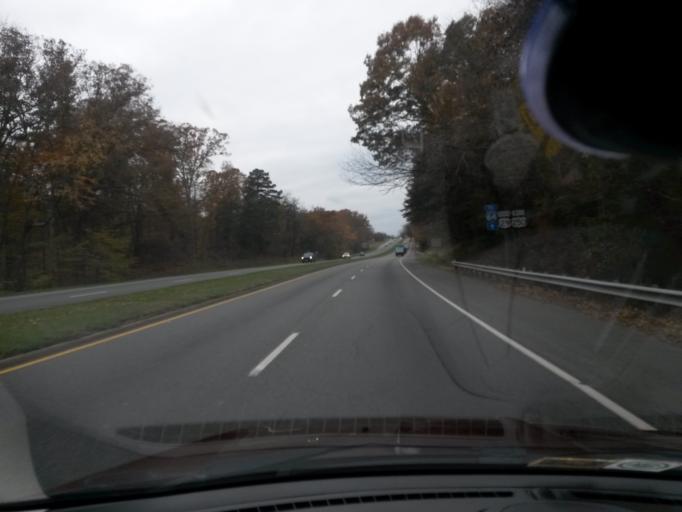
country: US
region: Virginia
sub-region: City of Charlottesville
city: Charlottesville
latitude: 38.0562
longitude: -78.5087
